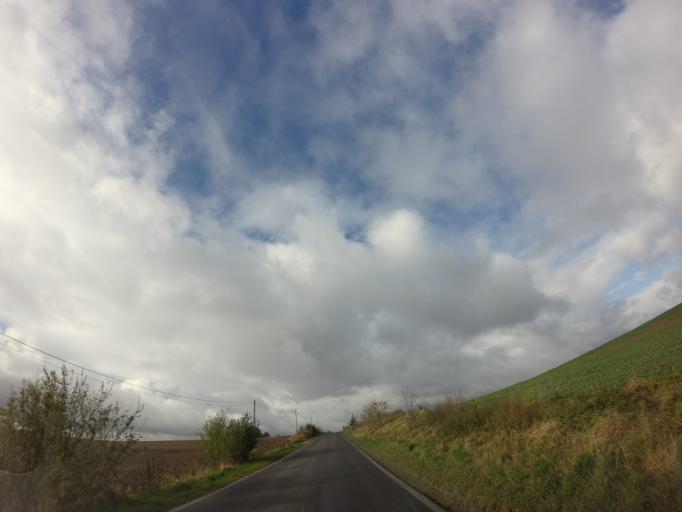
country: PL
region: West Pomeranian Voivodeship
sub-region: Powiat choszczenski
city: Pelczyce
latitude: 53.0361
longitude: 15.3253
